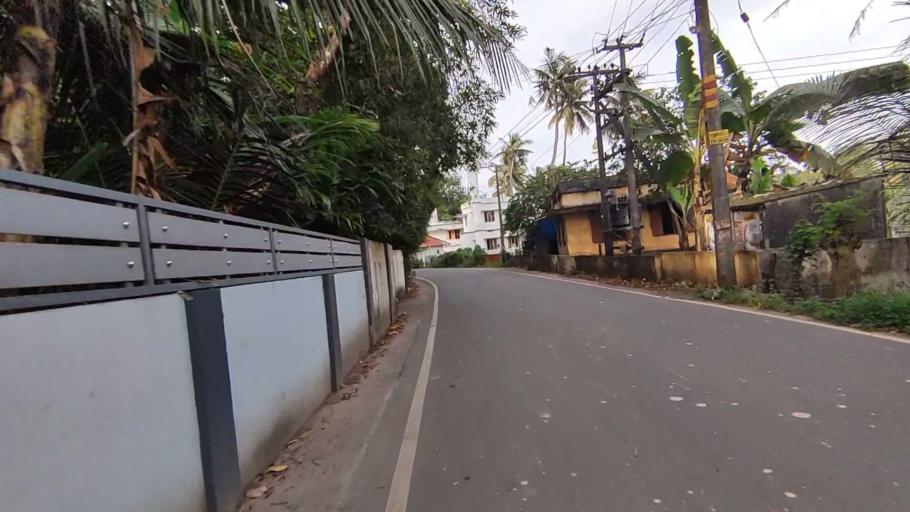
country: IN
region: Kerala
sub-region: Kottayam
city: Kottayam
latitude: 9.5985
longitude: 76.5036
